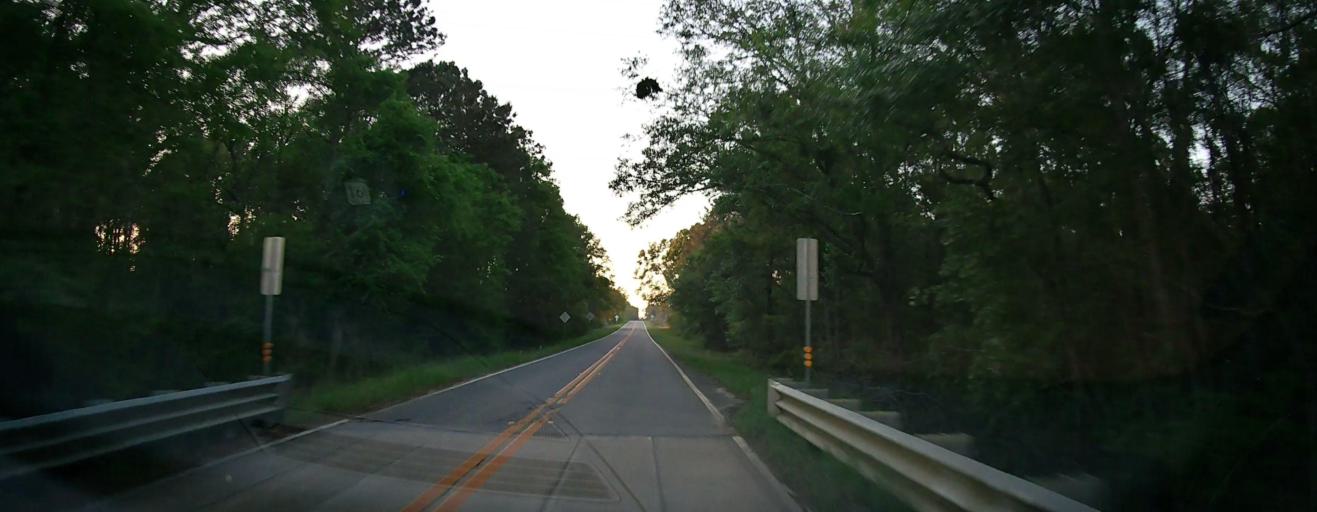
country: US
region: Georgia
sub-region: Wilcox County
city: Rochelle
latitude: 31.8016
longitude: -83.4532
